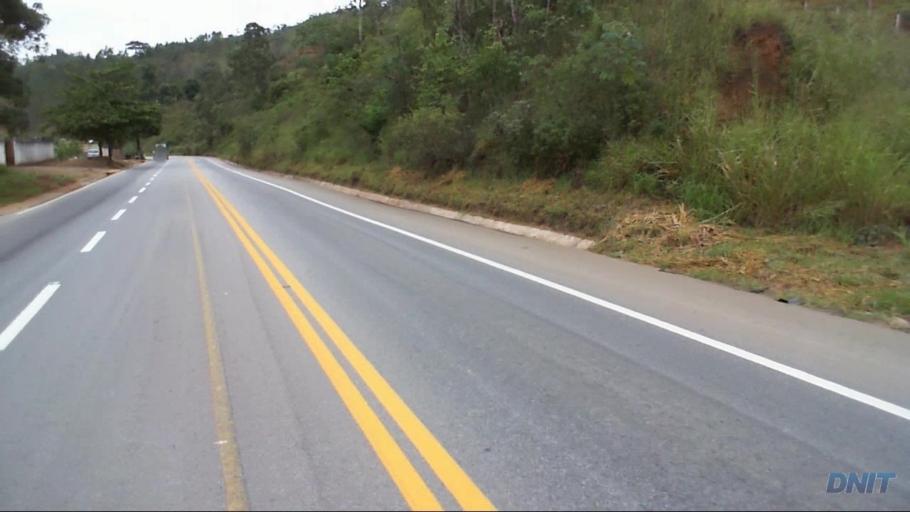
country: BR
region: Minas Gerais
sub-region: Timoteo
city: Timoteo
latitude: -19.6336
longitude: -42.8328
